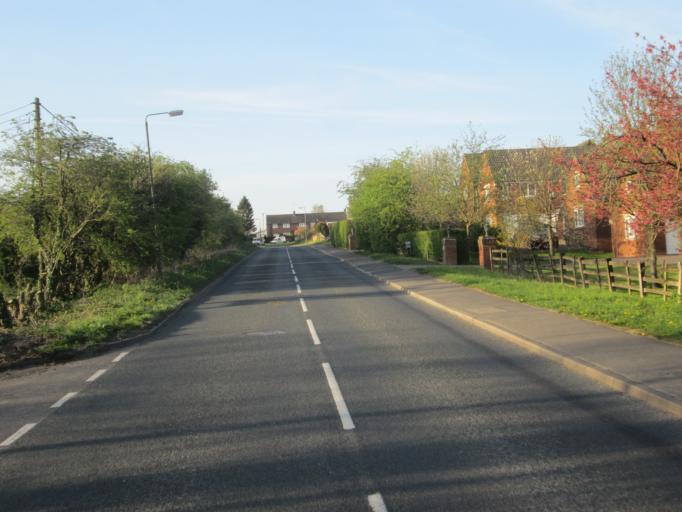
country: GB
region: England
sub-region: Derbyshire
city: Yeldersley
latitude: 52.9718
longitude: -1.6227
